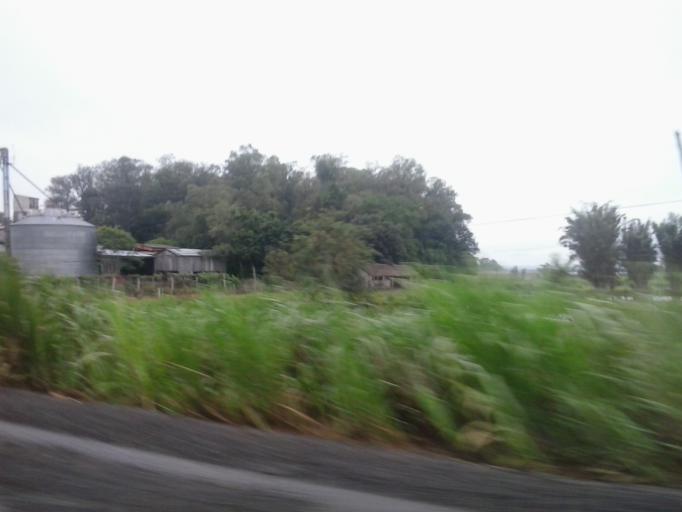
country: BR
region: Rio Grande do Sul
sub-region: Candelaria
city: Candelaria
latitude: -29.7302
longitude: -53.1941
